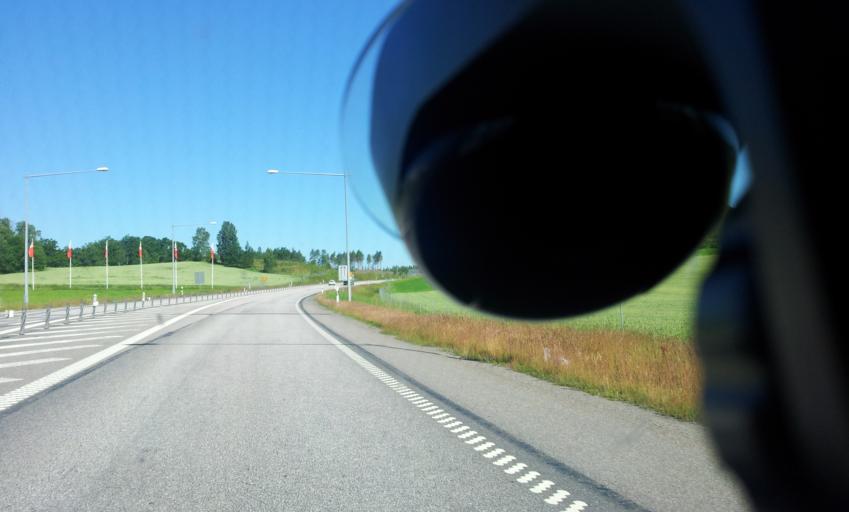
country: SE
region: OEstergoetland
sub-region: Valdemarsviks Kommun
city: Gusum
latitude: 58.3348
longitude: 16.4558
